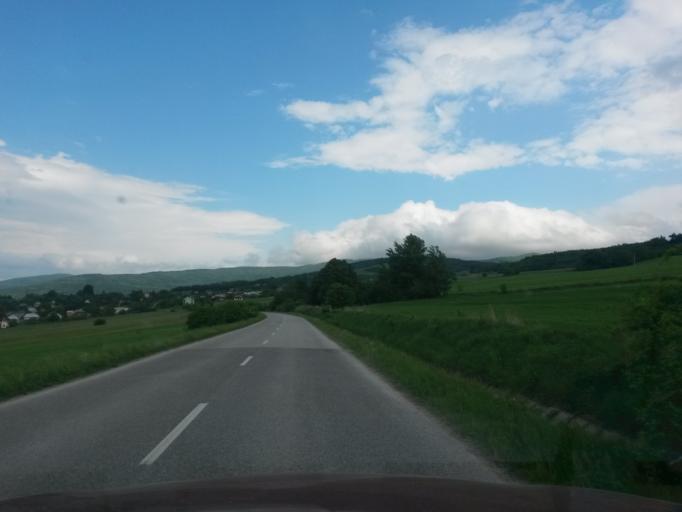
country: SK
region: Kosicky
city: Kosice
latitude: 48.7285
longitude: 21.1164
